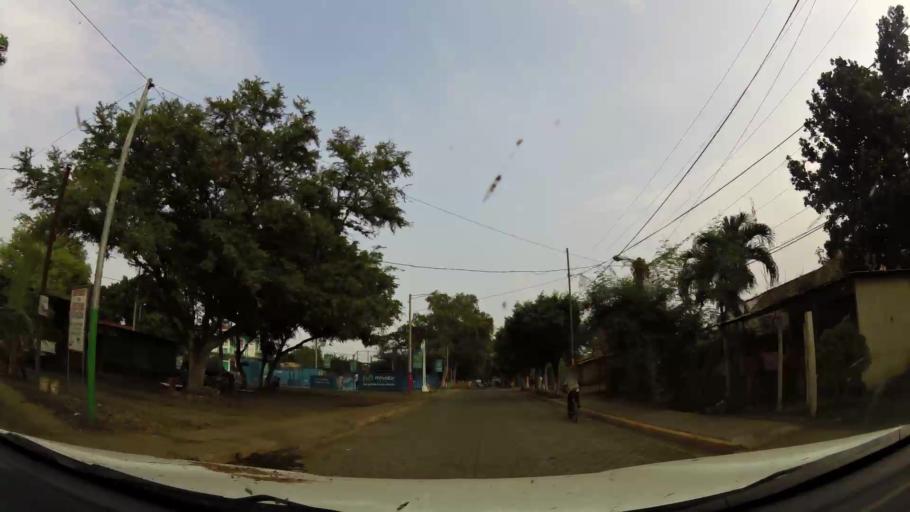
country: NI
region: Masaya
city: Masaya
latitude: 11.9834
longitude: -86.0981
